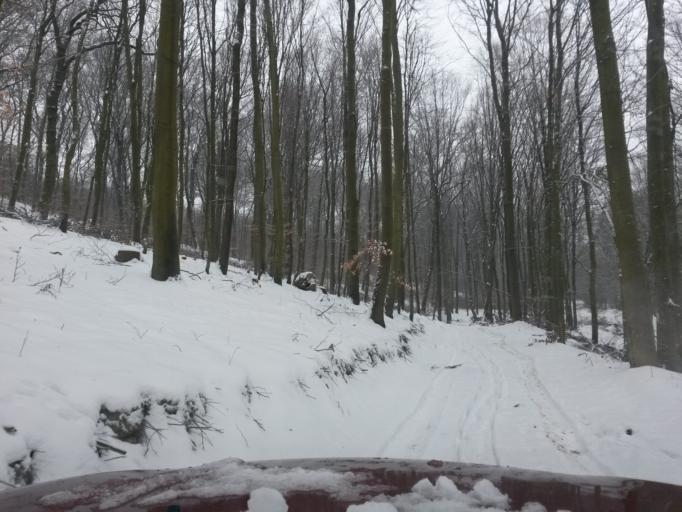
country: SK
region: Kosicky
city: Kosice
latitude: 48.7174
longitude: 21.3272
